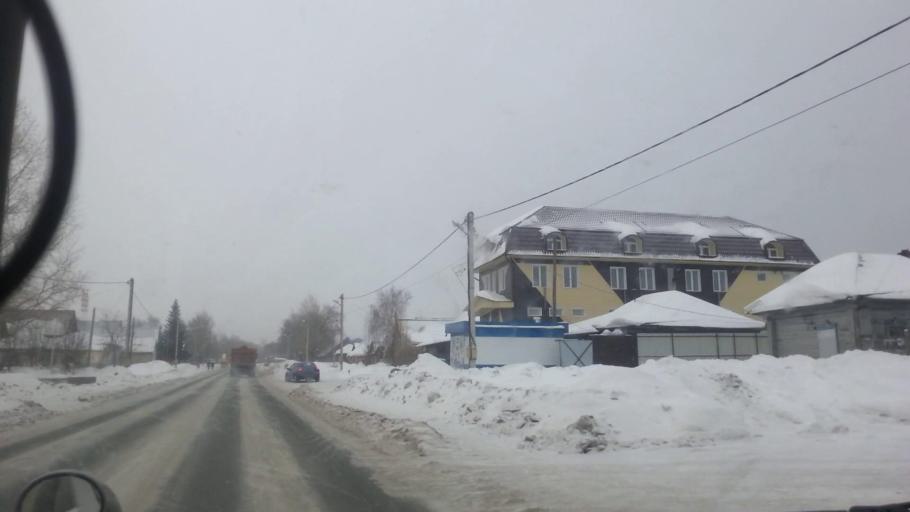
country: RU
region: Altai Krai
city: Vlasikha
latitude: 53.2982
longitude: 83.5873
